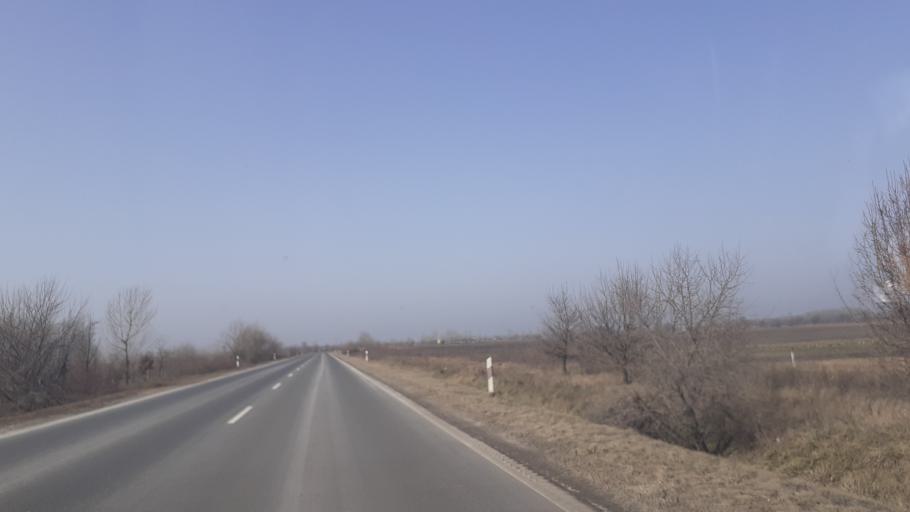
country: HU
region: Pest
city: Bugyi
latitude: 47.2172
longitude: 19.1352
